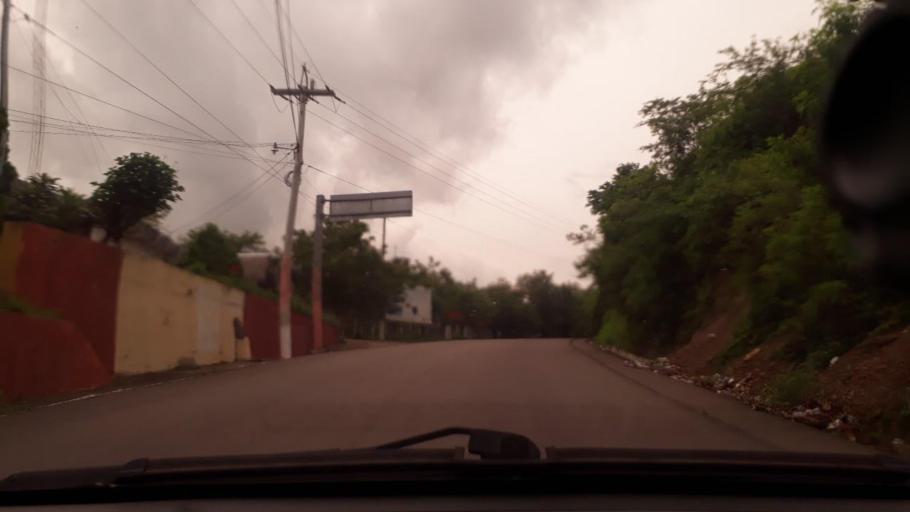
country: GT
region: Chiquimula
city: San Jacinto
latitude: 14.7328
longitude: -89.5020
